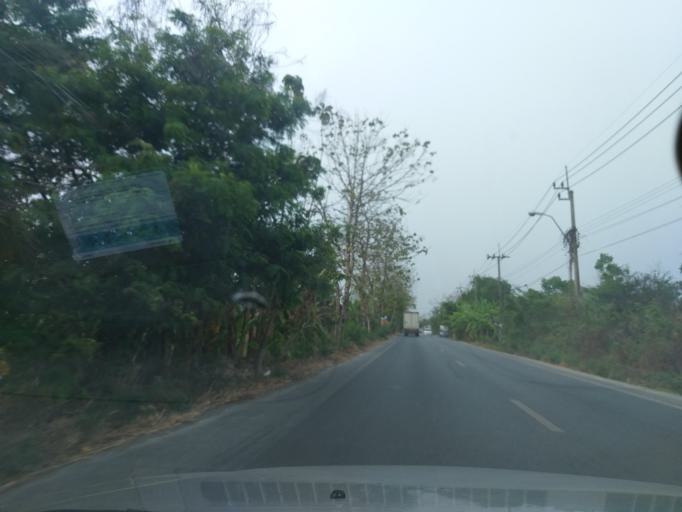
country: TH
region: Bangkok
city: Nong Chok
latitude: 13.9198
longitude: 100.8916
